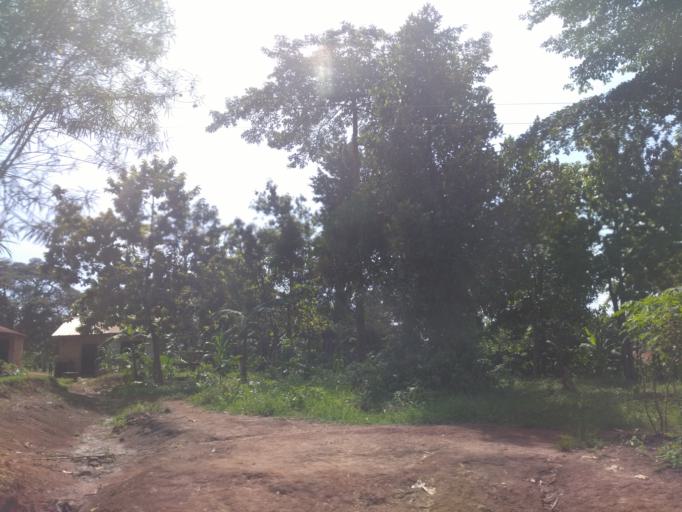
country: UG
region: Central Region
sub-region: Wakiso District
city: Kireka
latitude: 0.4488
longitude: 32.5825
